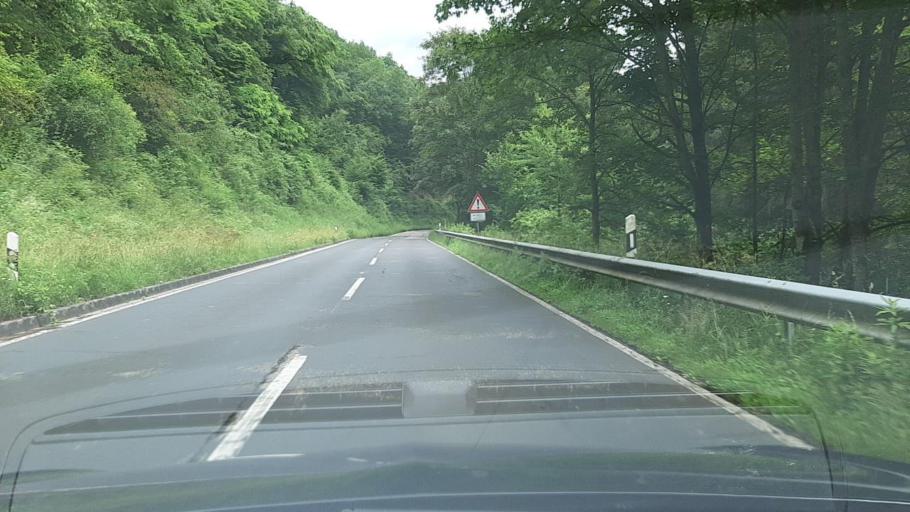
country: DE
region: Rheinland-Pfalz
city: Macken
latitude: 50.1861
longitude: 7.4116
